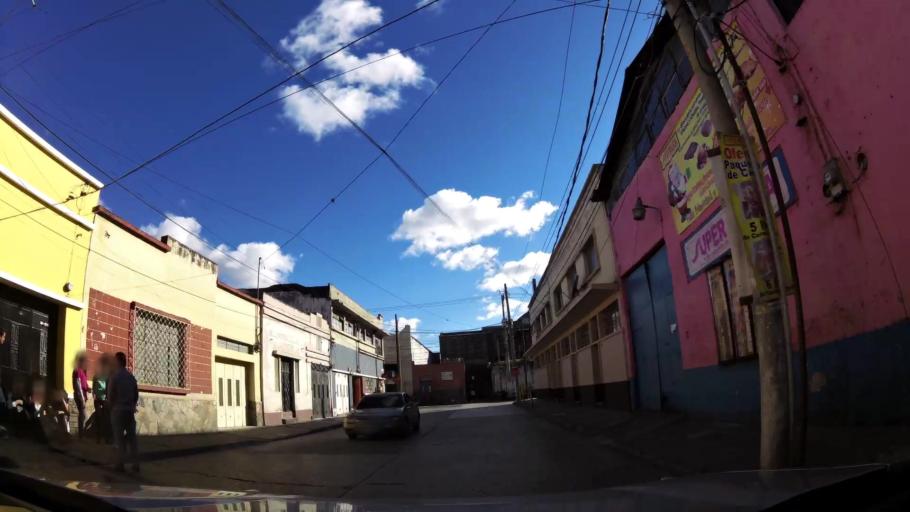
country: GT
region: Guatemala
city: Guatemala City
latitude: 14.6382
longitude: -90.5060
